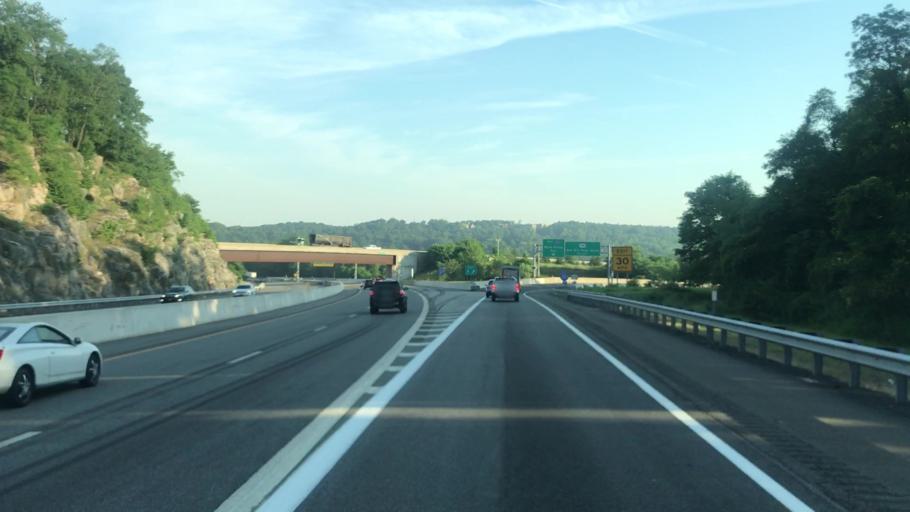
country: US
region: New York
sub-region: Westchester County
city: Elmsford
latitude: 41.0547
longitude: -73.8340
